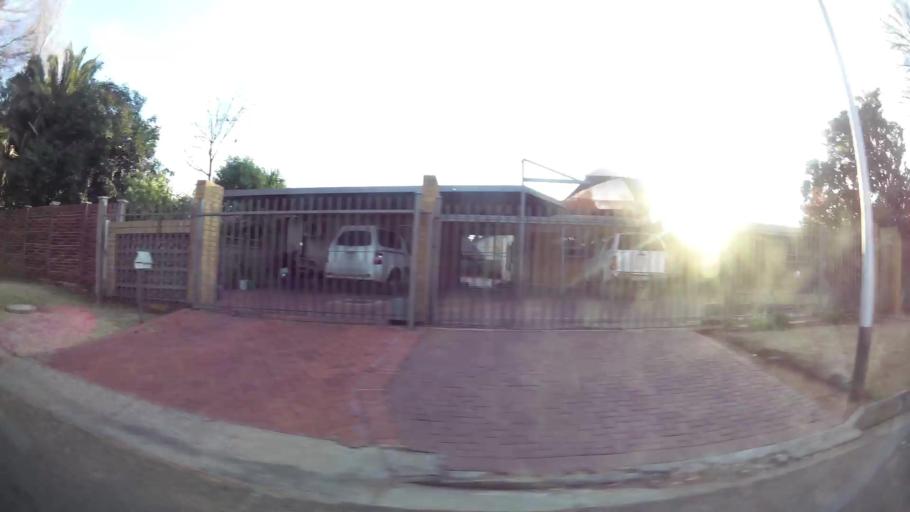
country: ZA
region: Orange Free State
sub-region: Mangaung Metropolitan Municipality
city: Bloemfontein
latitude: -29.1370
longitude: 26.1764
